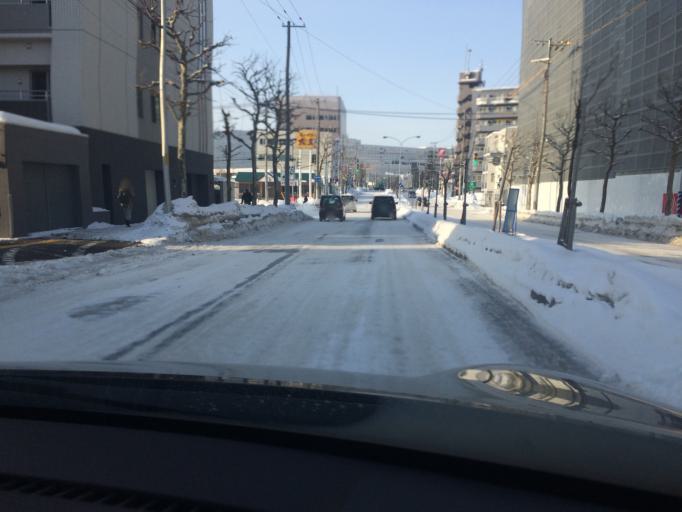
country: JP
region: Hokkaido
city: Ebetsu
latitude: 43.0413
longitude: 141.4774
